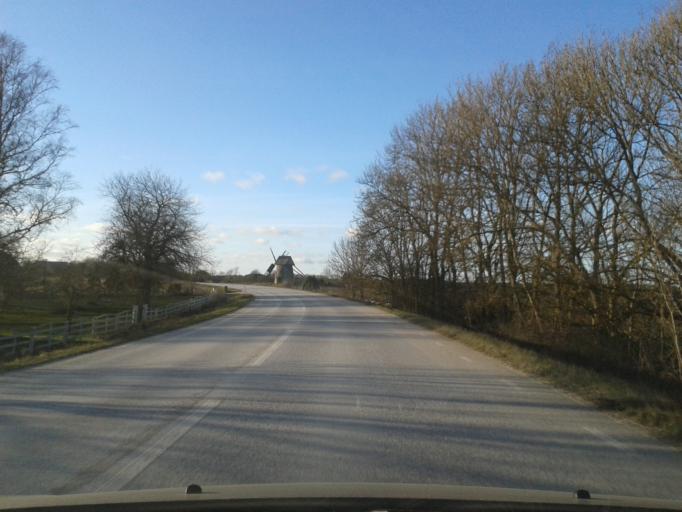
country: SE
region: Gotland
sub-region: Gotland
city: Slite
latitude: 57.4317
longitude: 18.6383
